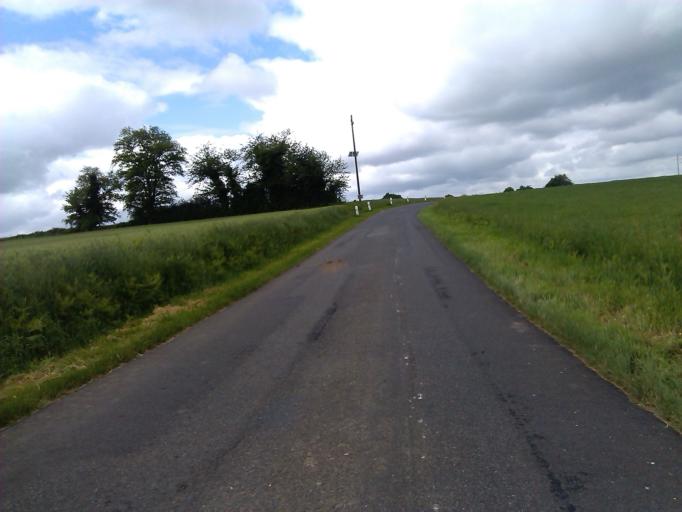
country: FR
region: Poitou-Charentes
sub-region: Departement de la Vienne
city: Availles-Limouzine
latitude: 46.1048
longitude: 0.5469
